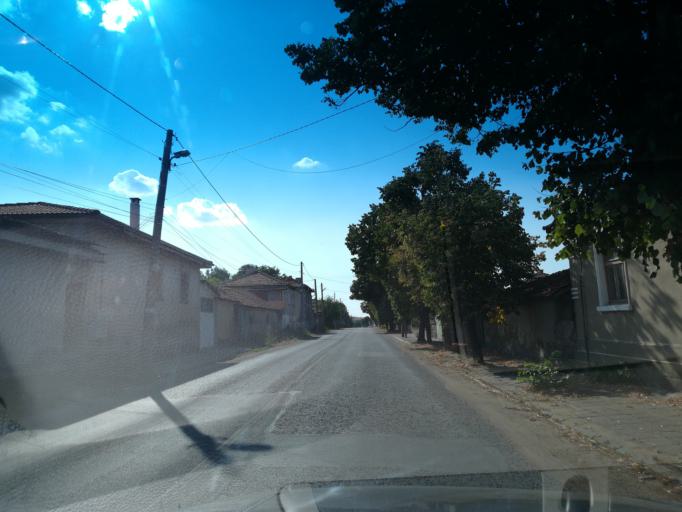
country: BG
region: Khaskovo
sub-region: Obshtina Mineralni Bani
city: Mineralni Bani
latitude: 42.0162
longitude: 25.4266
